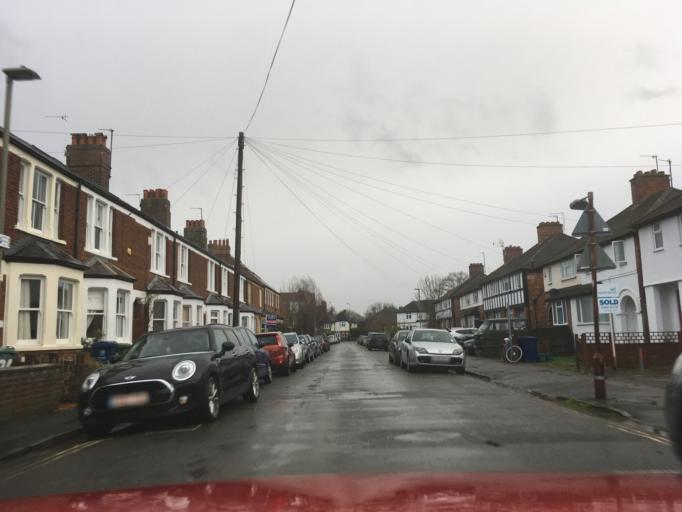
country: GB
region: England
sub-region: Oxfordshire
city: Oxford
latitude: 51.7536
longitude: -1.2793
